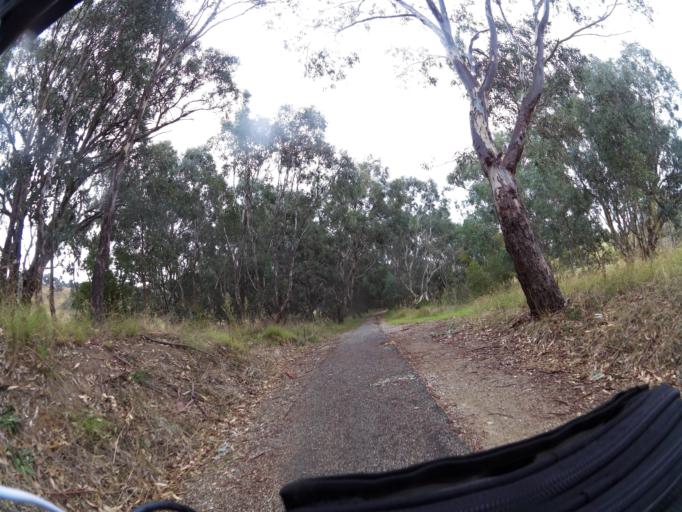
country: AU
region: New South Wales
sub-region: Albury Municipality
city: East Albury
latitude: -36.2254
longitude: 147.1264
